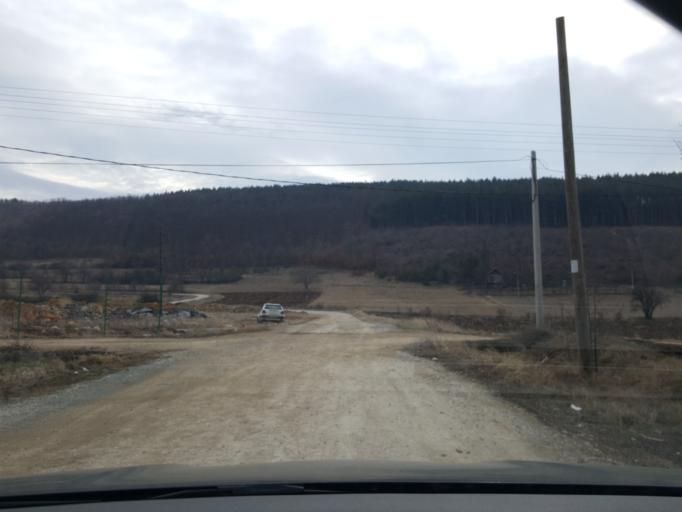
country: RS
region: Central Serbia
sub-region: Pirotski Okrug
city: Dimitrovgrad
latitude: 43.0109
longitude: 22.7468
